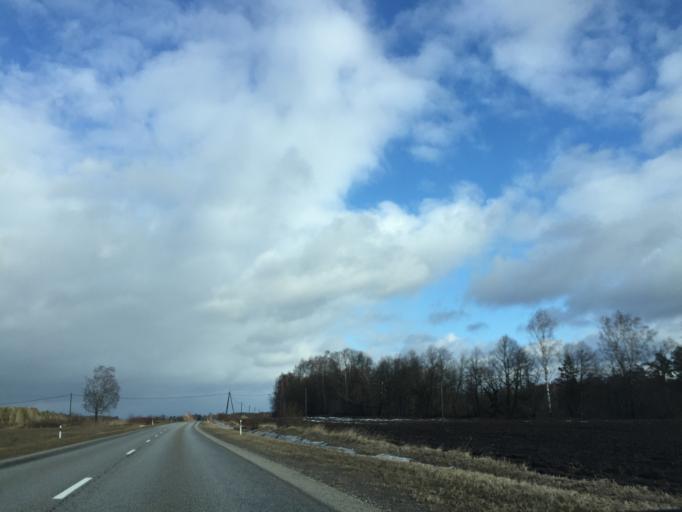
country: LV
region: Aloja
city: Staicele
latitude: 57.8765
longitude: 24.5842
